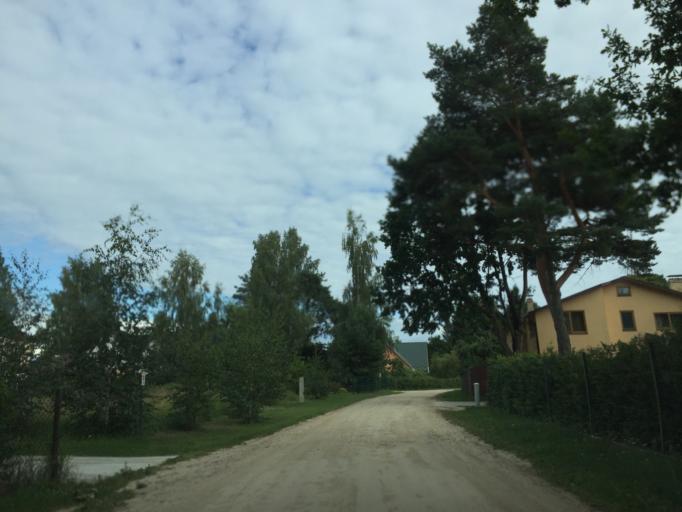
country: LV
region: Riga
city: Jaunciems
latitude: 57.1033
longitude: 24.1932
